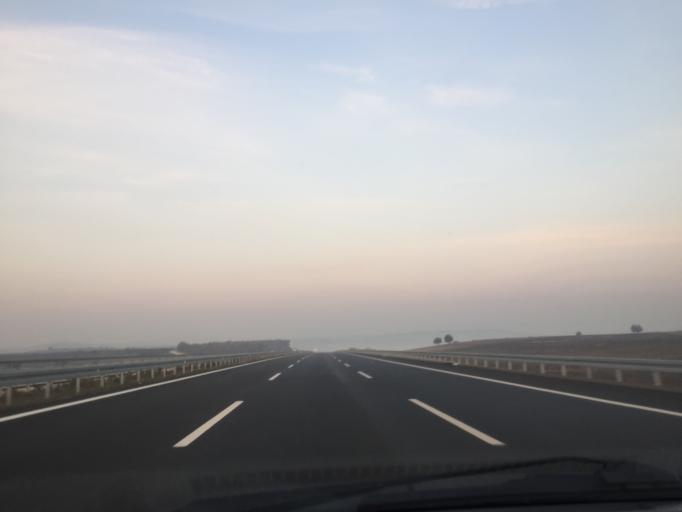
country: TR
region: Bursa
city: Mahmudiye
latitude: 40.2580
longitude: 28.6898
